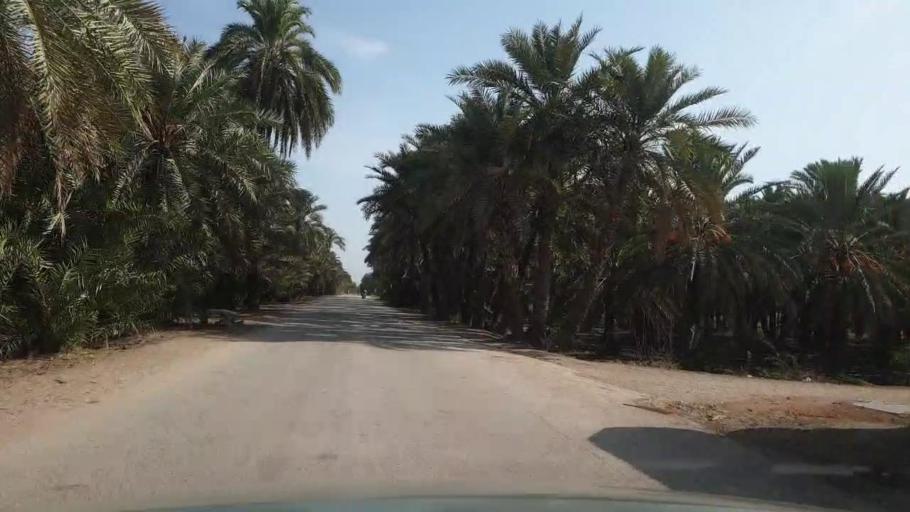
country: PK
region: Sindh
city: Rohri
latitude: 27.6681
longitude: 68.8781
